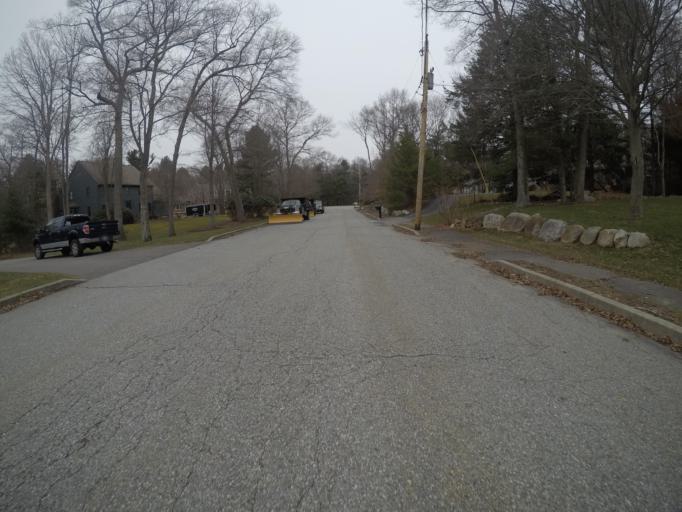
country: US
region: Massachusetts
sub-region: Bristol County
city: Easton
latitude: 42.0605
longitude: -71.1461
